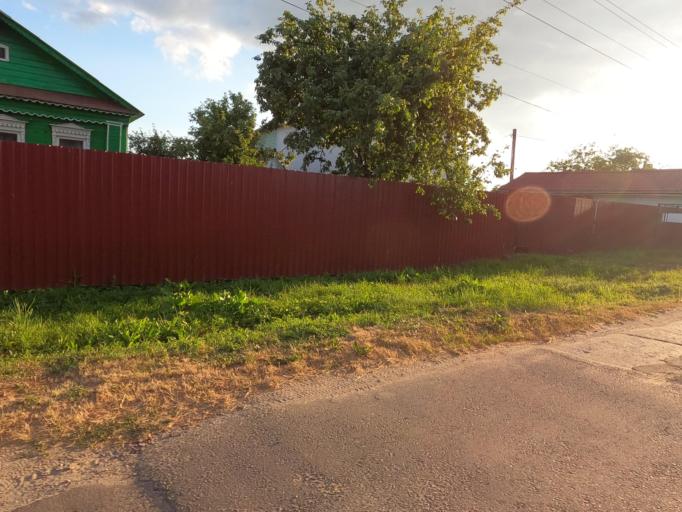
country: RU
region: Moskovskaya
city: Ashitkovo
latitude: 55.4198
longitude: 38.5763
